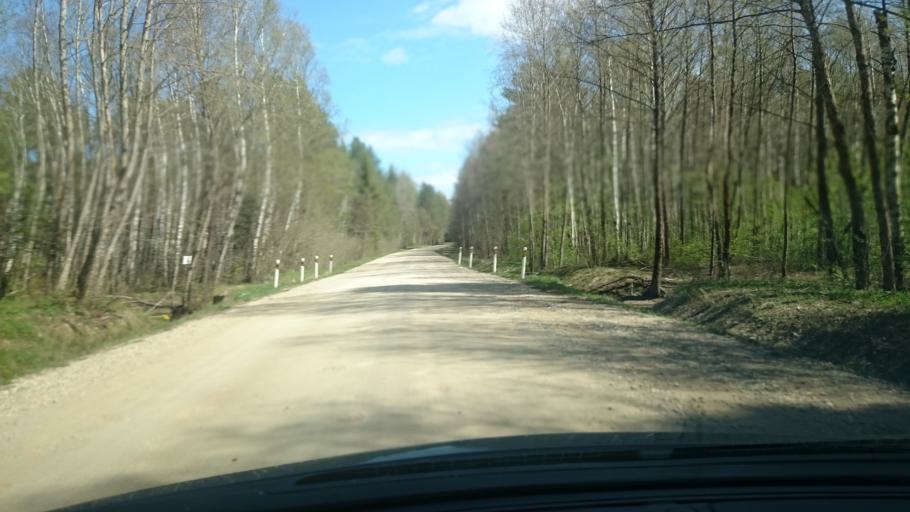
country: EE
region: Ida-Virumaa
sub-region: Sillamaee linn
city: Sillamae
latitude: 59.0816
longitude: 27.7365
